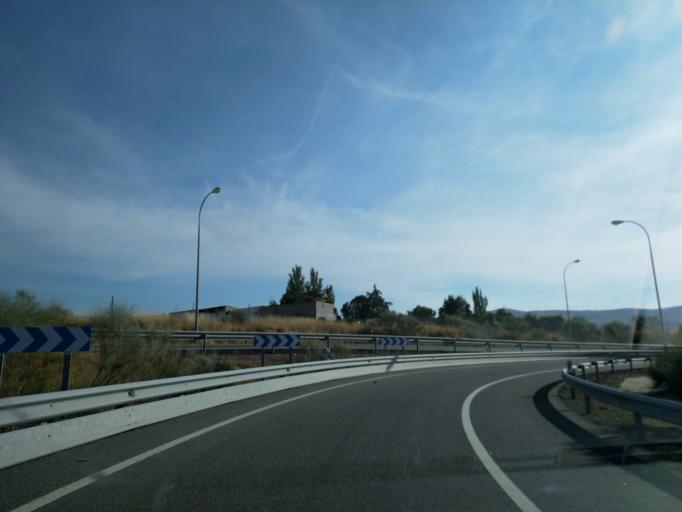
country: ES
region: Castille and Leon
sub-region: Provincia de Segovia
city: Villacastin
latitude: 40.7721
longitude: -4.4202
